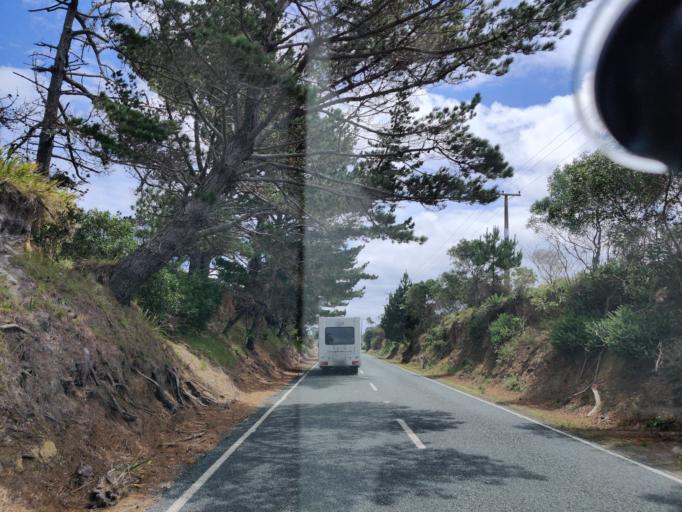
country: NZ
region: Northland
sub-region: Far North District
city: Kaitaia
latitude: -34.7781
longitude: 173.0937
